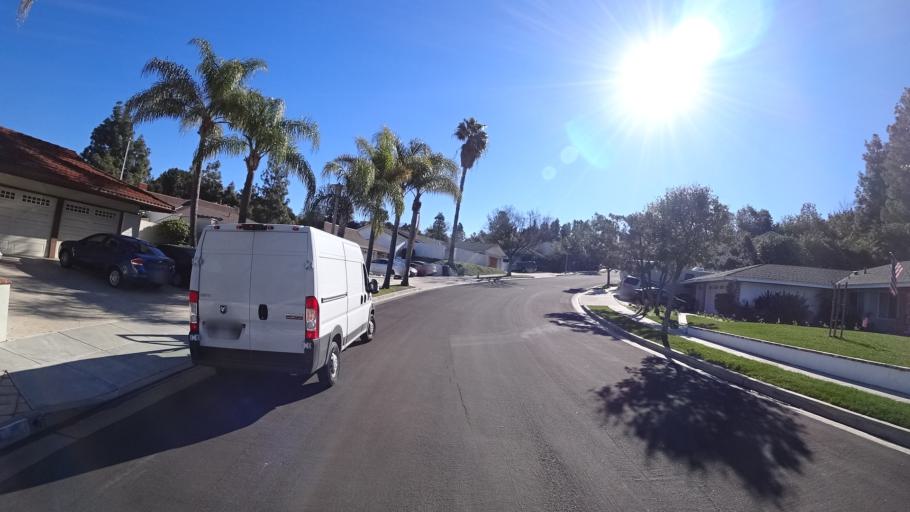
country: US
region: California
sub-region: Orange County
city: Villa Park
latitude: 33.8407
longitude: -117.8286
